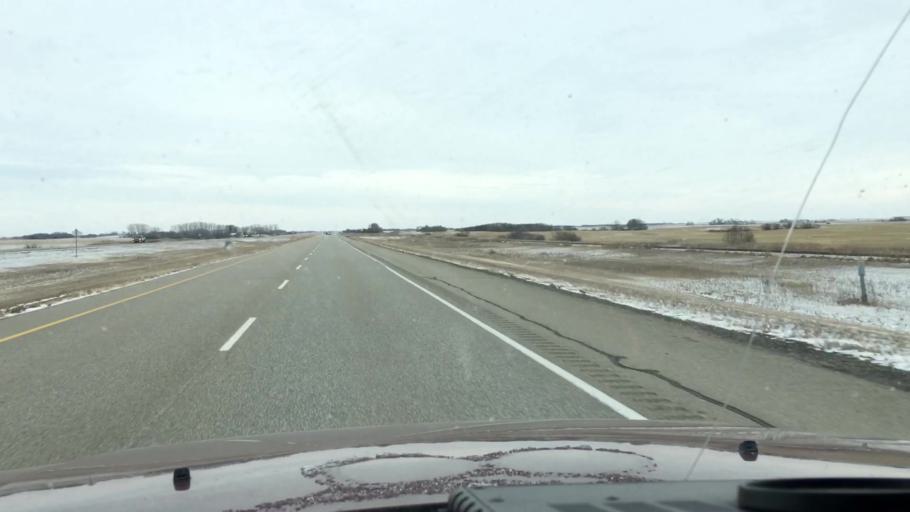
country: CA
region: Saskatchewan
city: Watrous
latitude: 51.3494
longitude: -106.1151
